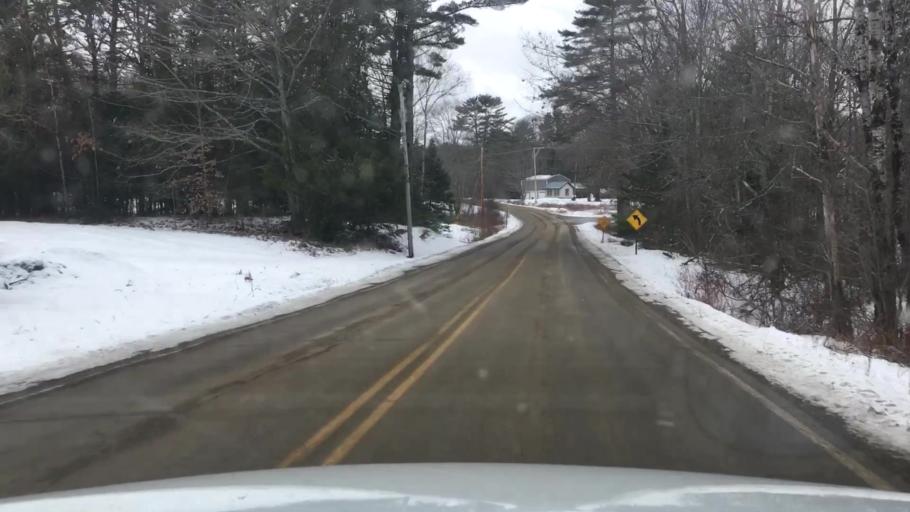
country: US
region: Maine
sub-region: Waldo County
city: Lincolnville
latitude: 44.2883
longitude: -69.0280
